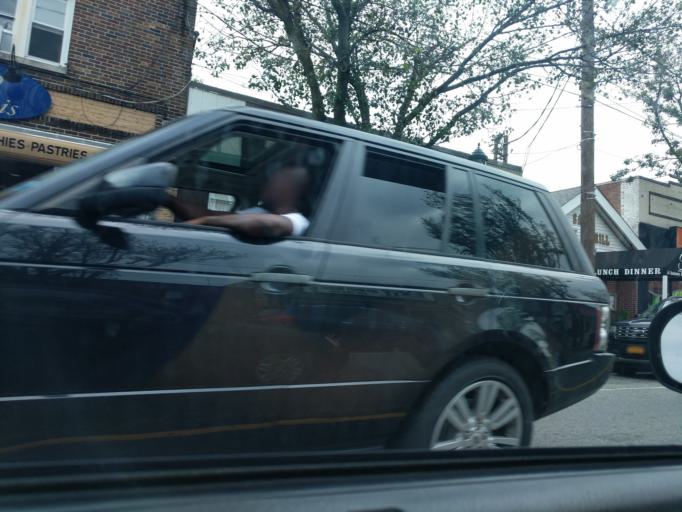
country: US
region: New York
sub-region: Nassau County
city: Valley Stream
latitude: 40.6638
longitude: -73.6984
